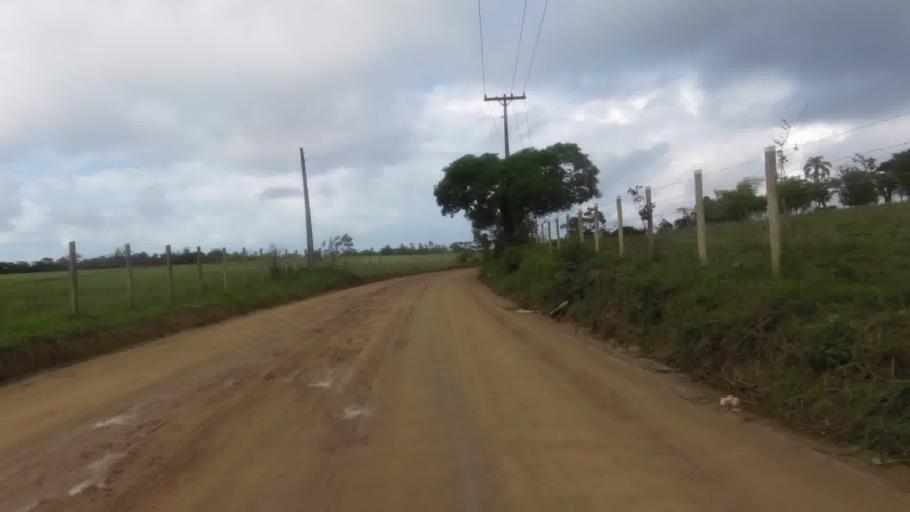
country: BR
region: Espirito Santo
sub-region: Piuma
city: Piuma
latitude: -20.7793
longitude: -40.6300
